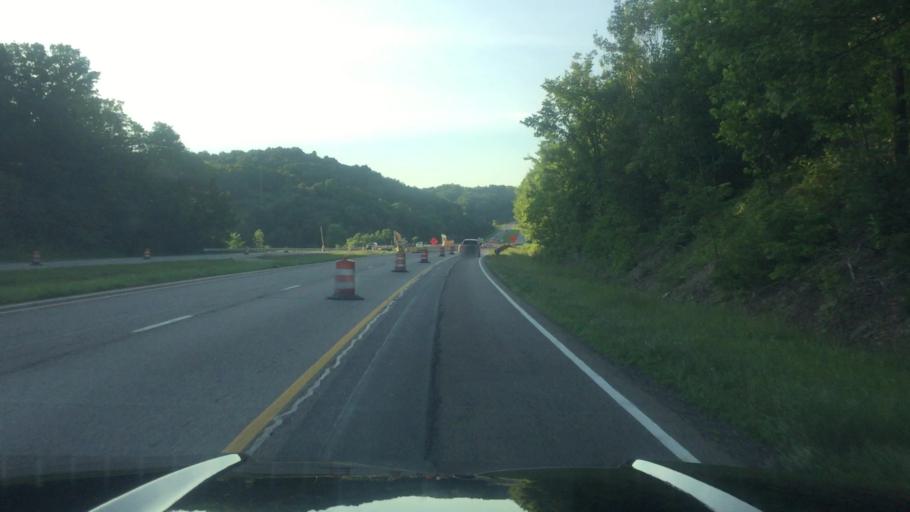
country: US
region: Ohio
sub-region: Tuscarawas County
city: Newcomerstown
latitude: 40.1780
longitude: -81.5534
